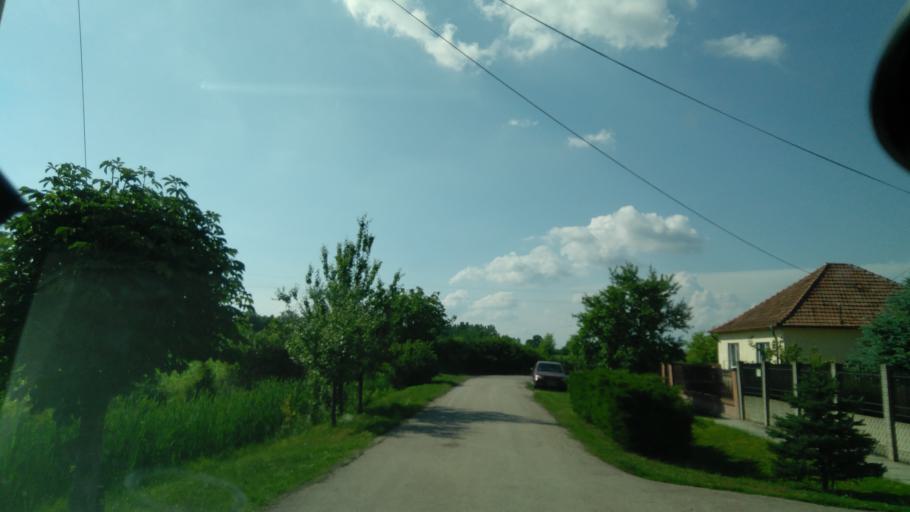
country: HU
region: Bekes
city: Bekes
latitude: 46.7043
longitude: 21.1759
